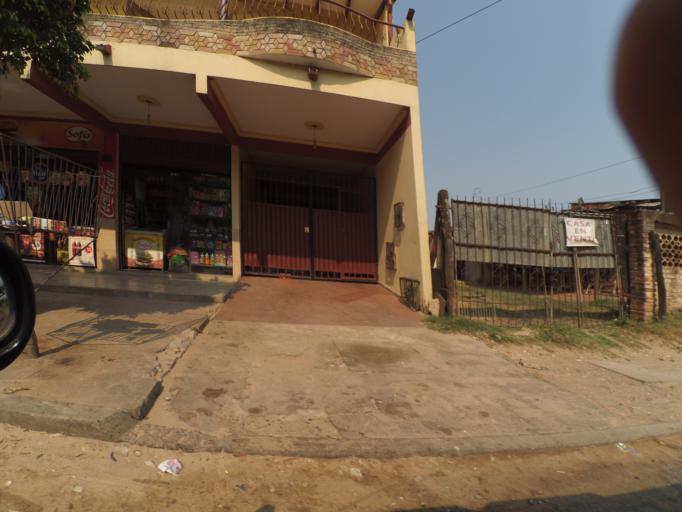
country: BO
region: Santa Cruz
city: Santa Cruz de la Sierra
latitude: -17.8309
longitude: -63.2263
